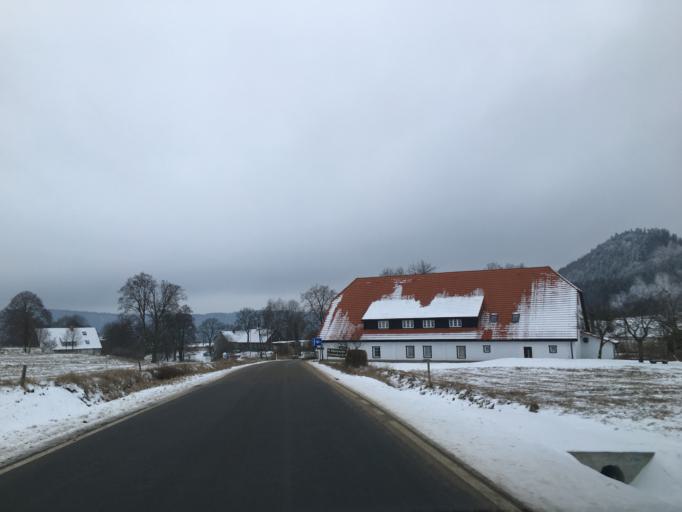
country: PL
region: Lower Silesian Voivodeship
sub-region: Powiat walbrzyski
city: Mieroszow
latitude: 50.6735
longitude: 16.1575
